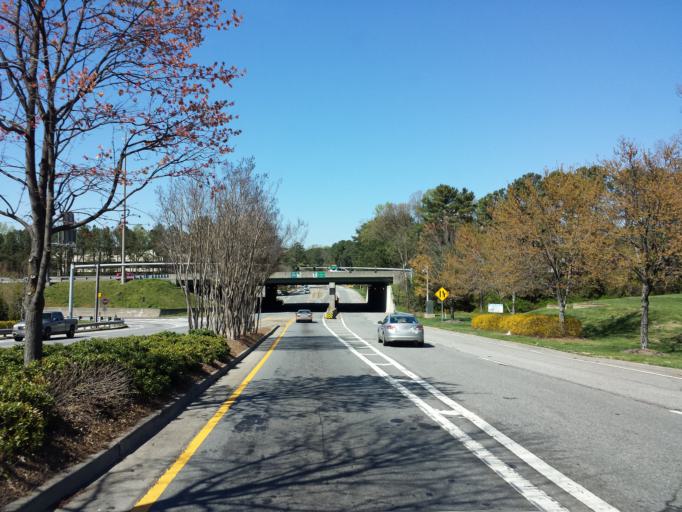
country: US
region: Georgia
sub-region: Fulton County
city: Sandy Springs
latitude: 33.9090
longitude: -84.3617
